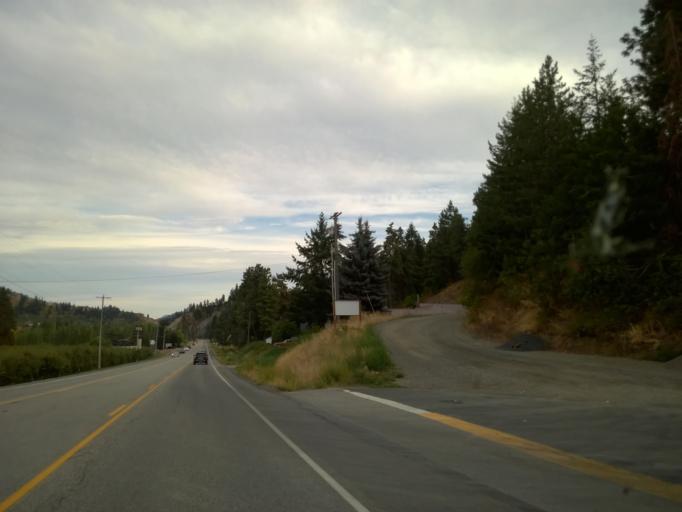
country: US
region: Washington
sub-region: Chelan County
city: Leavenworth
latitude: 47.5902
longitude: -120.6302
